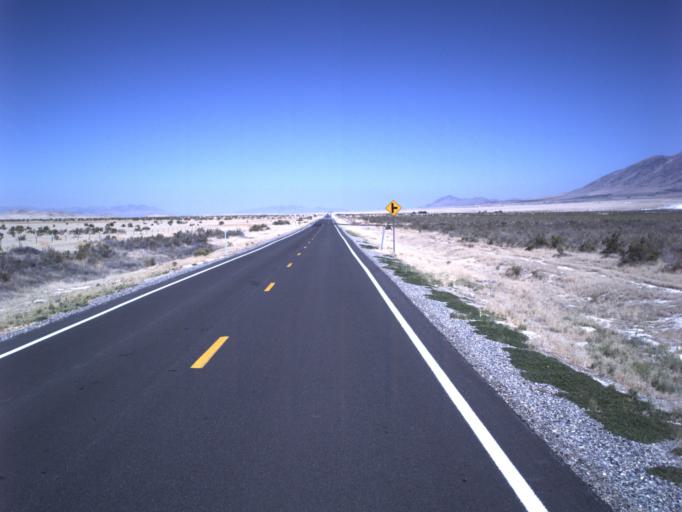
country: US
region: Utah
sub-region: Tooele County
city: Grantsville
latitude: 40.3043
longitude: -112.7430
